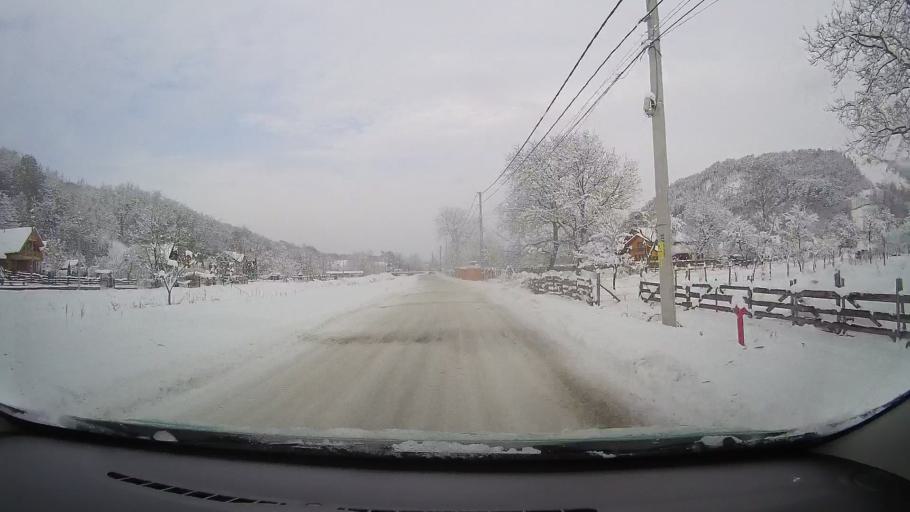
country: RO
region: Alba
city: Pianu de Sus
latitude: 45.8874
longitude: 23.4882
